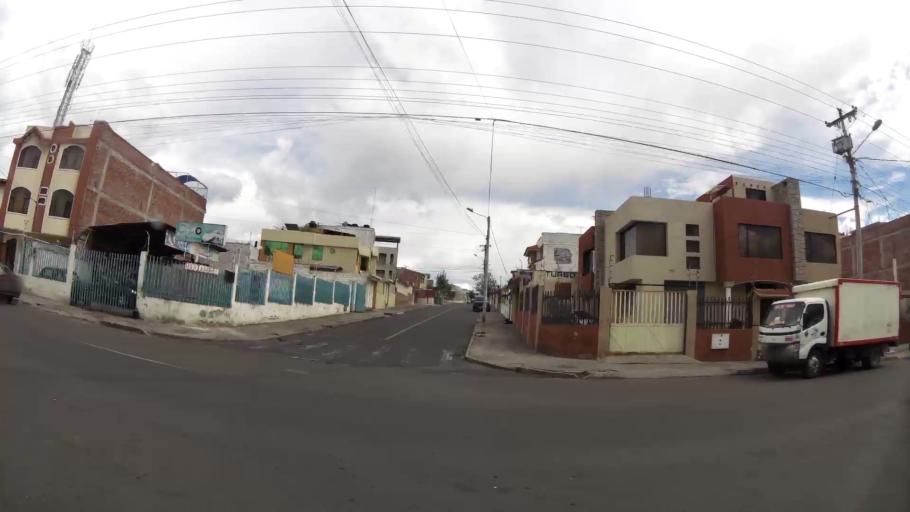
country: EC
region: Tungurahua
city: Ambato
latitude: -1.2553
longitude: -78.6310
